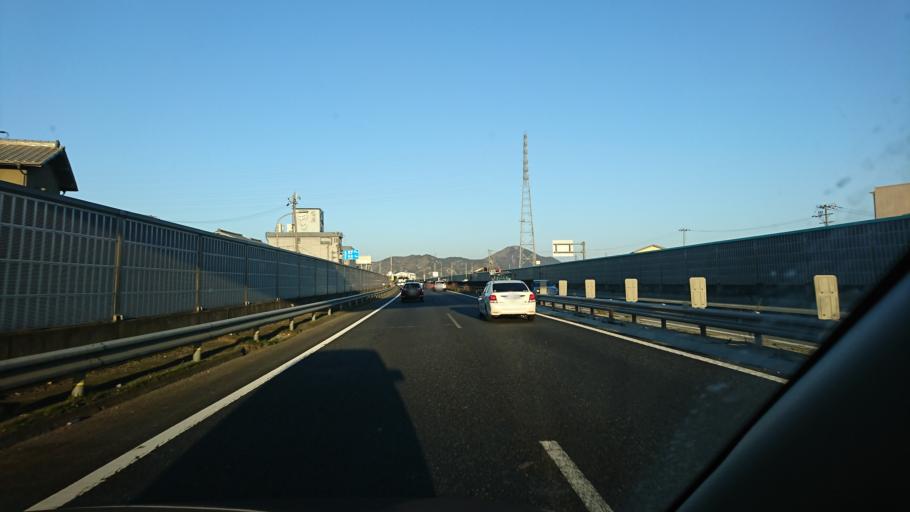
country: JP
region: Hyogo
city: Kakogawacho-honmachi
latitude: 34.7835
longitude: 134.8293
